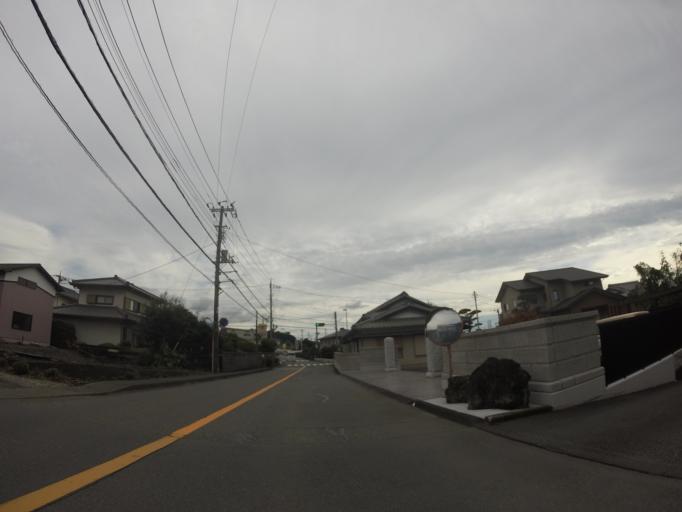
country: JP
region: Shizuoka
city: Fuji
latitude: 35.1891
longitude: 138.6918
